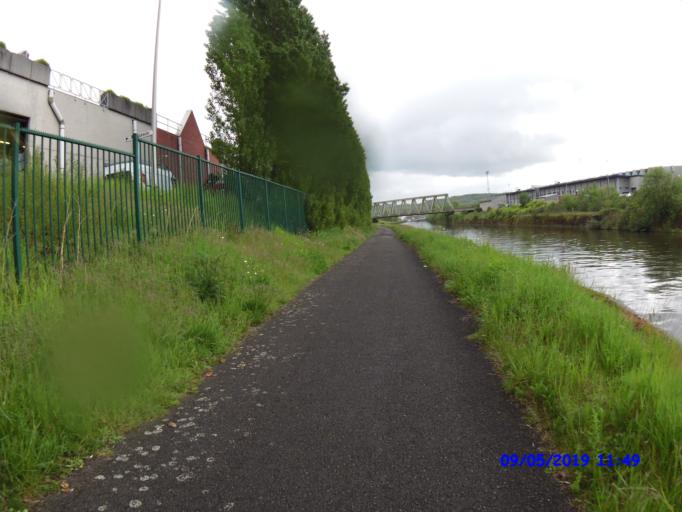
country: BE
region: Wallonia
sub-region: Province du Hainaut
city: Charleroi
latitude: 50.4022
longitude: 4.4569
